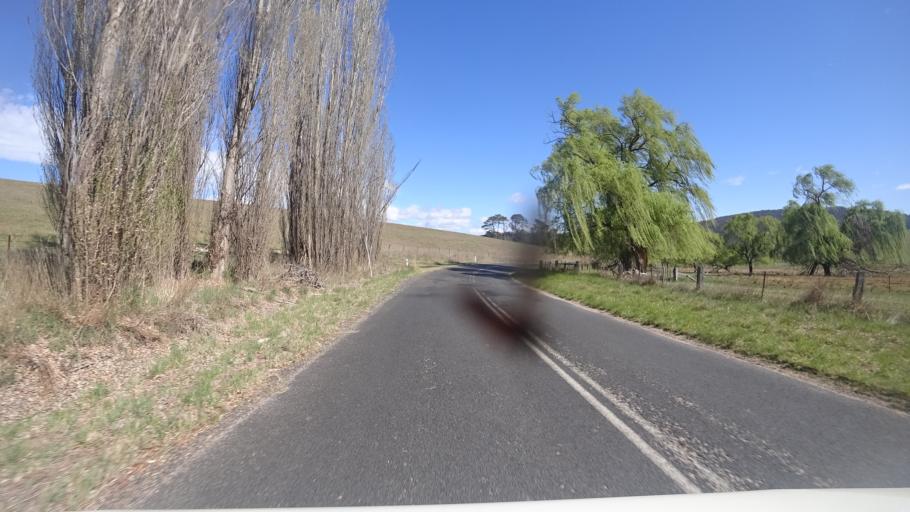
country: AU
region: New South Wales
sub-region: Lithgow
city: Bowenfels
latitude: -33.5186
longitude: 149.9602
